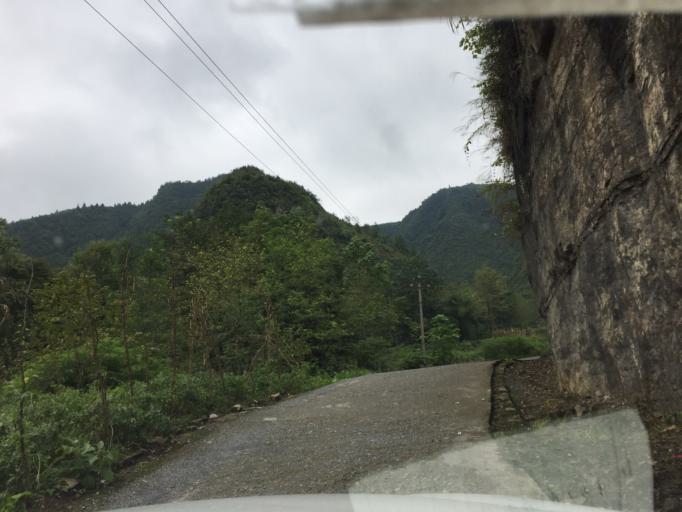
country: CN
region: Guizhou Sheng
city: Longquan
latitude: 28.2023
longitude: 108.0541
